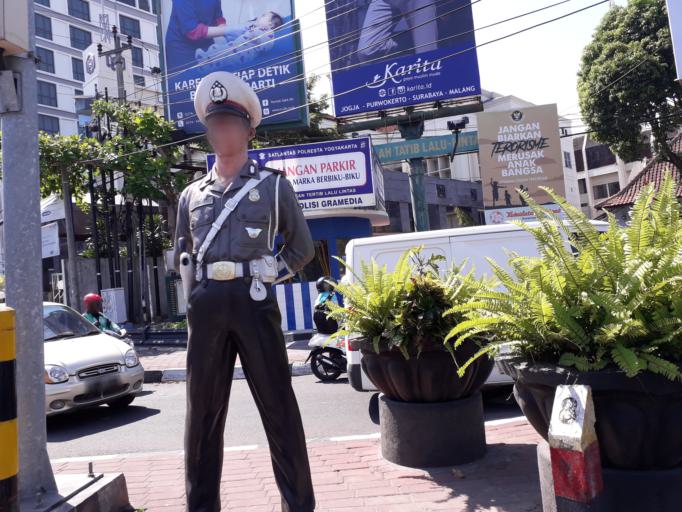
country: ID
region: Daerah Istimewa Yogyakarta
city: Yogyakarta
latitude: -7.7830
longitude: 110.3750
